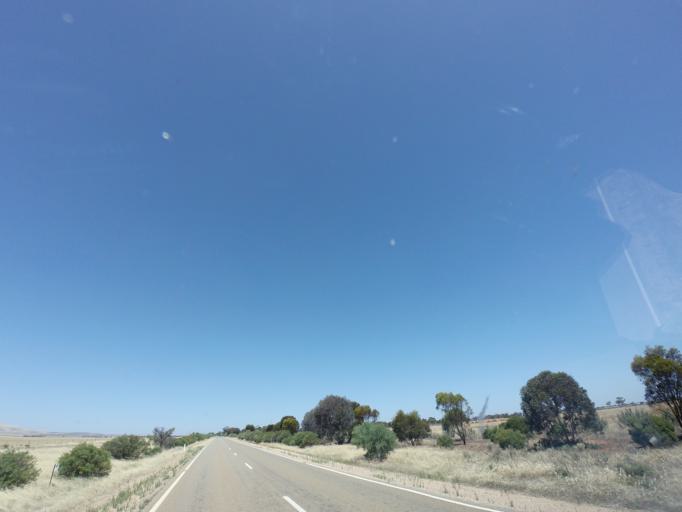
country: AU
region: South Australia
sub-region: Flinders Ranges
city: Quorn
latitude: -32.6851
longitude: 138.3205
